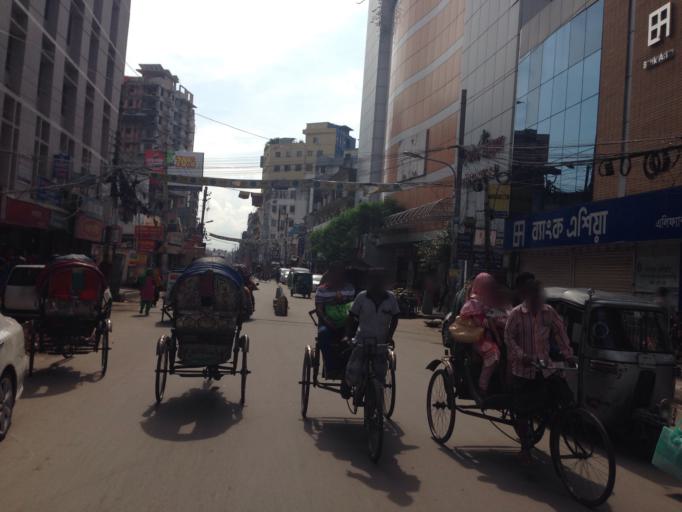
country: BD
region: Dhaka
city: Azimpur
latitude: 23.7372
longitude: 90.3868
